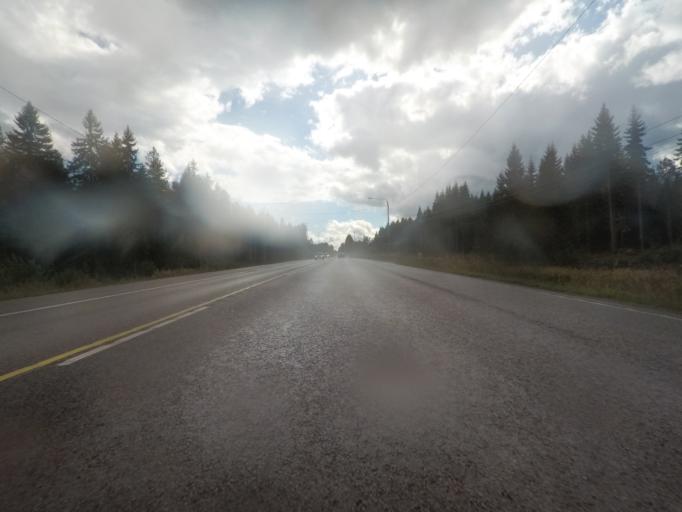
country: FI
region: Central Finland
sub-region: Joutsa
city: Leivonmaeki
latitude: 61.9011
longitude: 26.1157
